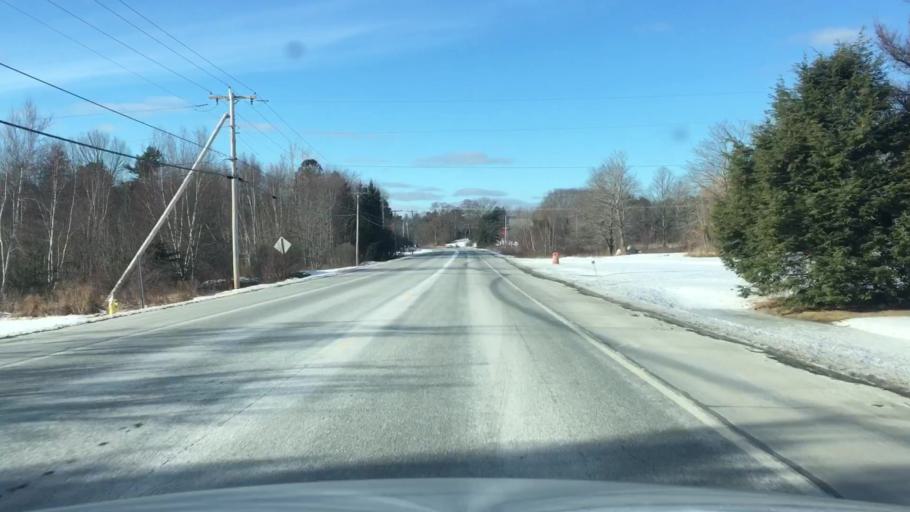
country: US
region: Maine
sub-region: Penobscot County
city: Holden
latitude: 44.7996
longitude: -68.5958
